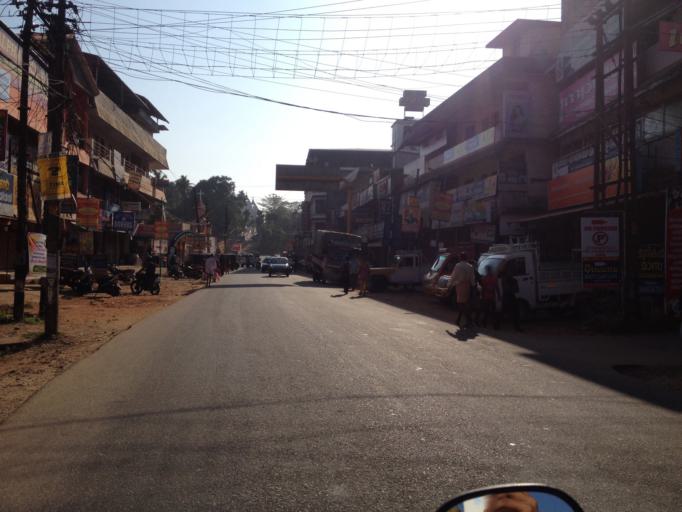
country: IN
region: Kerala
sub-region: Kollam
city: Punalur
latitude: 9.0054
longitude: 76.7842
